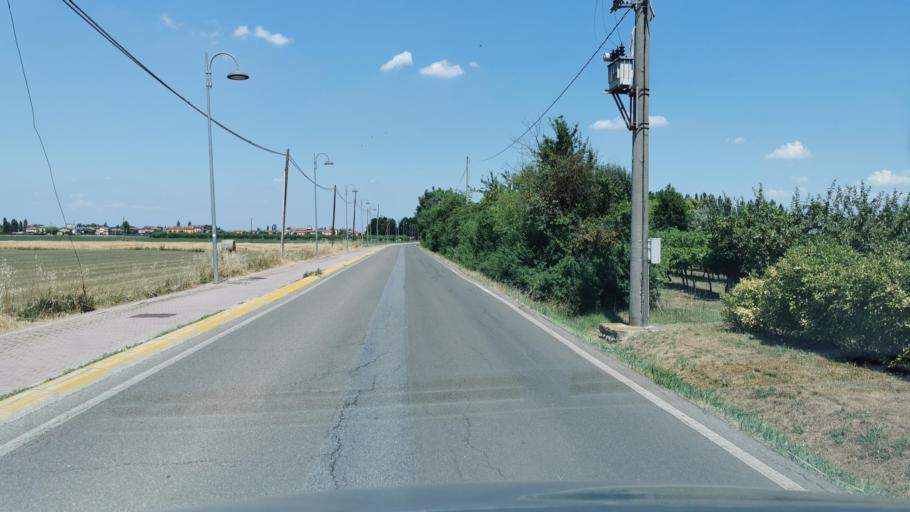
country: IT
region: Emilia-Romagna
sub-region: Provincia di Modena
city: Fossoli
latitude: 44.8086
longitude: 10.8889
